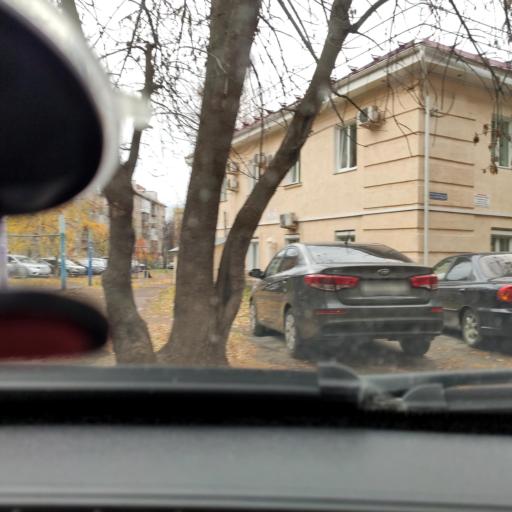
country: RU
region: Bashkortostan
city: Ufa
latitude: 54.7366
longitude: 55.9708
